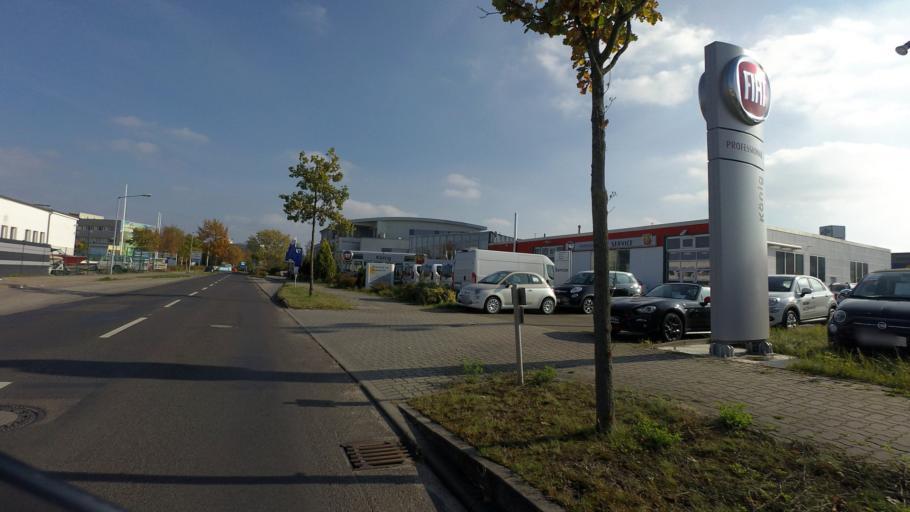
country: DE
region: Brandenburg
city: Erkner
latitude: 52.3975
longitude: 13.7177
